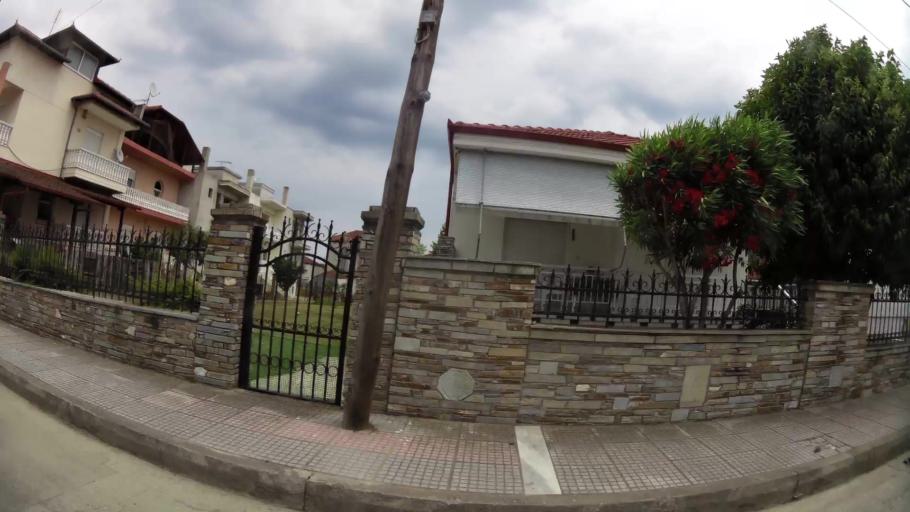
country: GR
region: Central Macedonia
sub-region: Nomos Pierias
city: Kallithea
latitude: 40.2759
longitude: 22.5835
